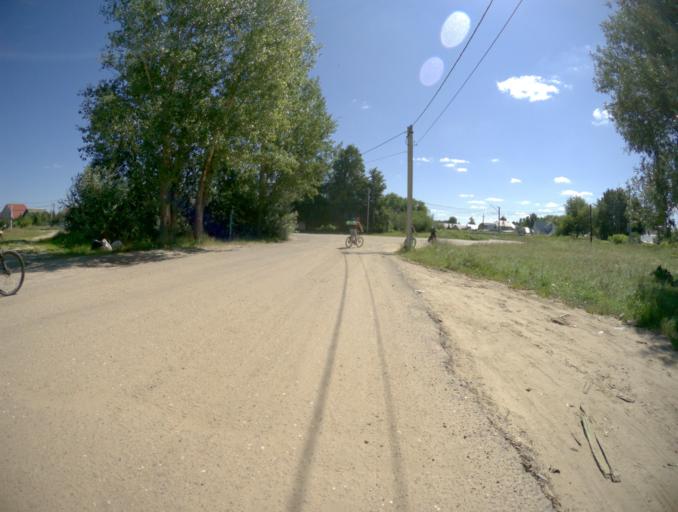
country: RU
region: Nizjnij Novgorod
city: Bor
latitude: 56.3720
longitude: 44.0538
